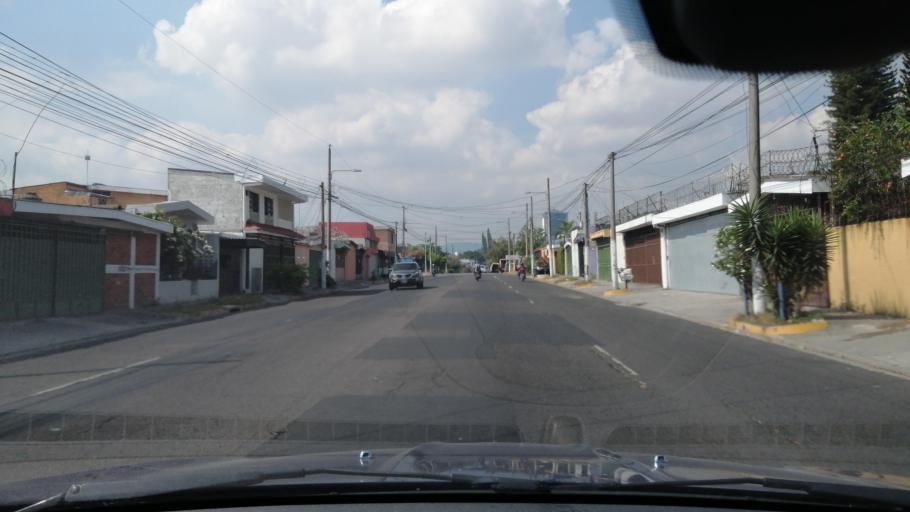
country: SV
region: San Salvador
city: Mejicanos
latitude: 13.7118
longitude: -89.2184
